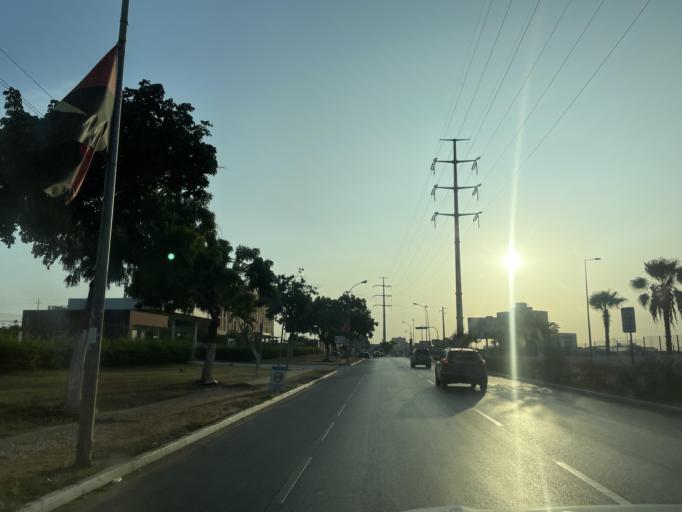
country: AO
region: Luanda
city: Luanda
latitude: -8.9136
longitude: 13.1958
